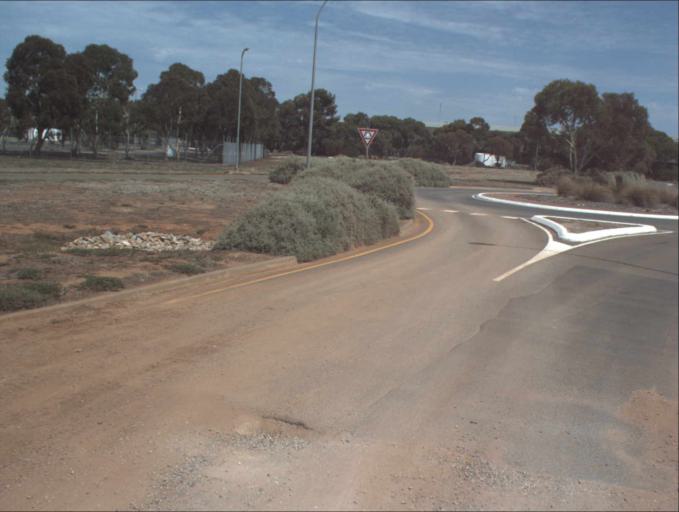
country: AU
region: South Australia
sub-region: Port Adelaide Enfield
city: Enfield
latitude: -34.8400
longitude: 138.6139
